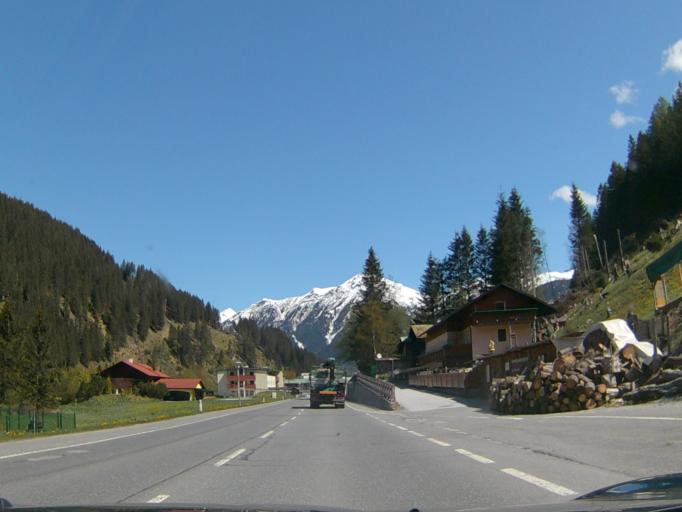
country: AT
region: Salzburg
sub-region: Politischer Bezirk Sankt Johann im Pongau
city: Bad Gastein
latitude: 47.0985
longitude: 13.1263
